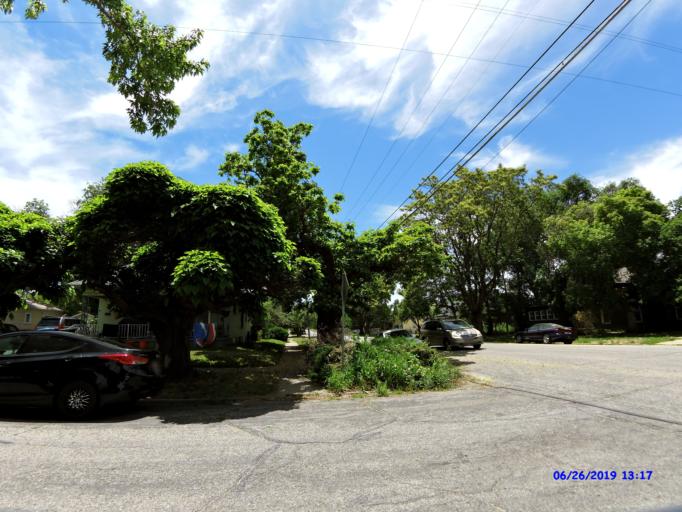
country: US
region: Utah
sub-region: Weber County
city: South Ogden
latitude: 41.2080
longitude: -111.9651
